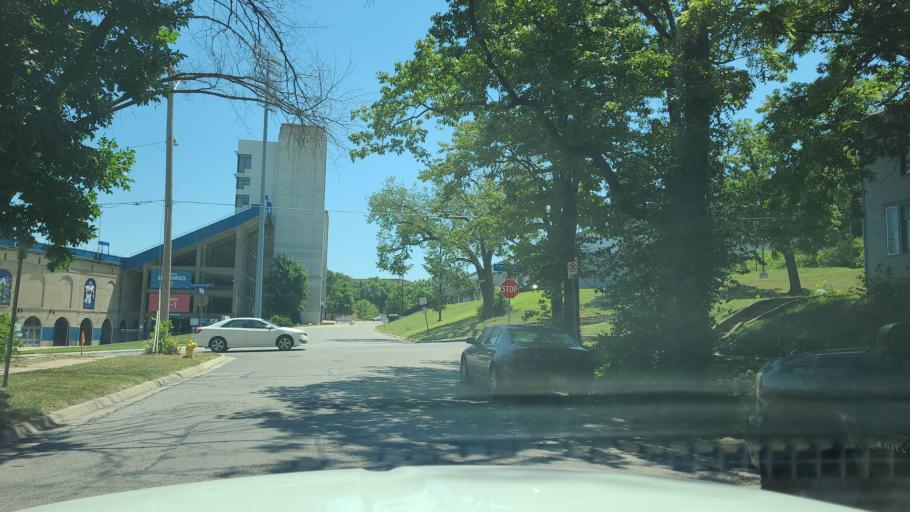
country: US
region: Kansas
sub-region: Douglas County
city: Lawrence
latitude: 38.9646
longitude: -95.2476
